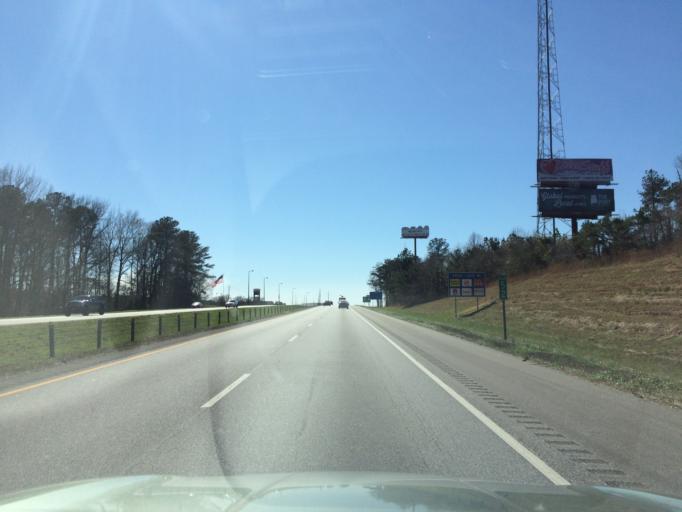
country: US
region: Alabama
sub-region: Lee County
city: Auburn
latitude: 32.5636
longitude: -85.4971
